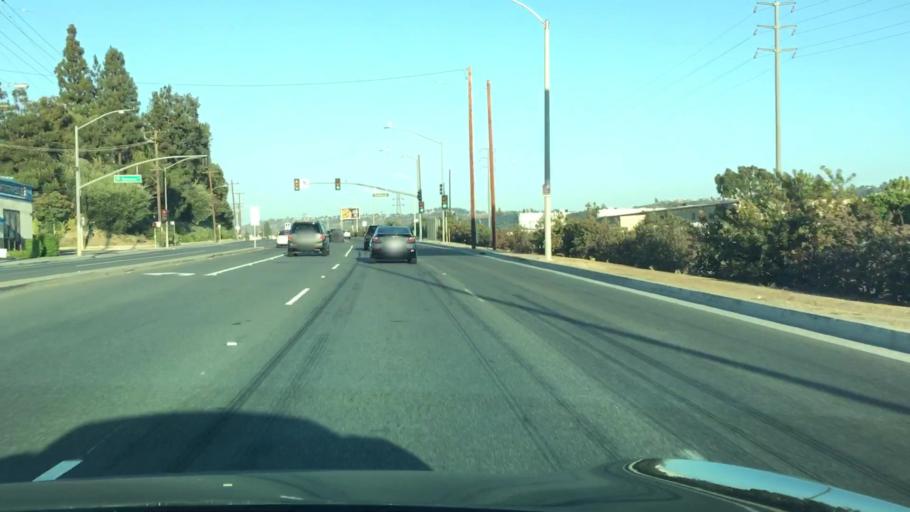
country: US
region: California
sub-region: Los Angeles County
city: Walnut
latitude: 34.0020
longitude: -117.8820
